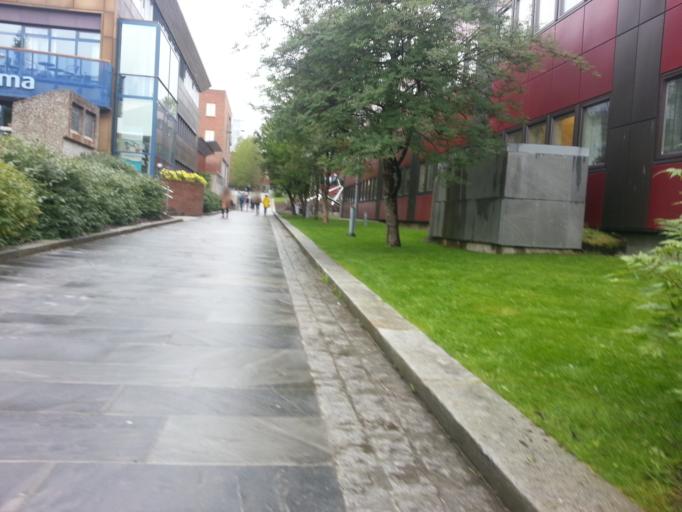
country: NO
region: Troms
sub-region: Tromso
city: Tromso
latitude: 69.6816
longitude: 18.9757
